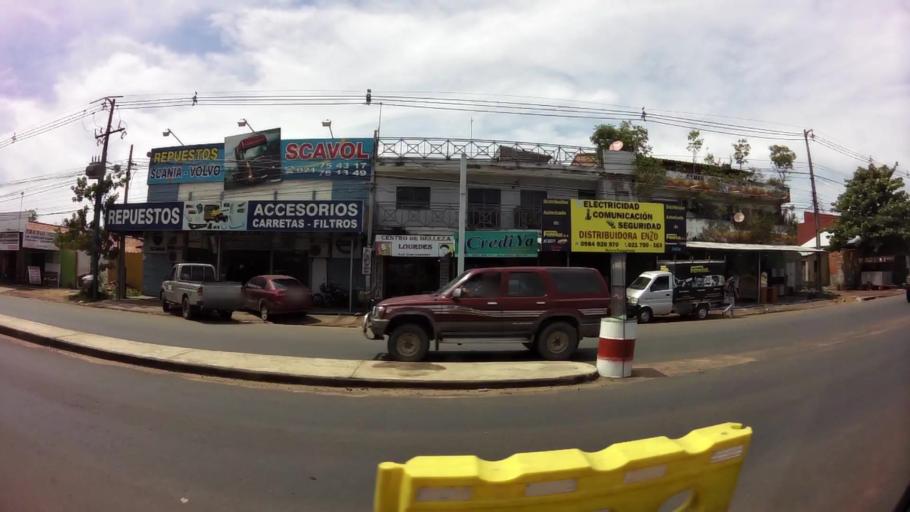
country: PY
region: Central
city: Colonia Mariano Roque Alonso
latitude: -25.2051
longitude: -57.5257
